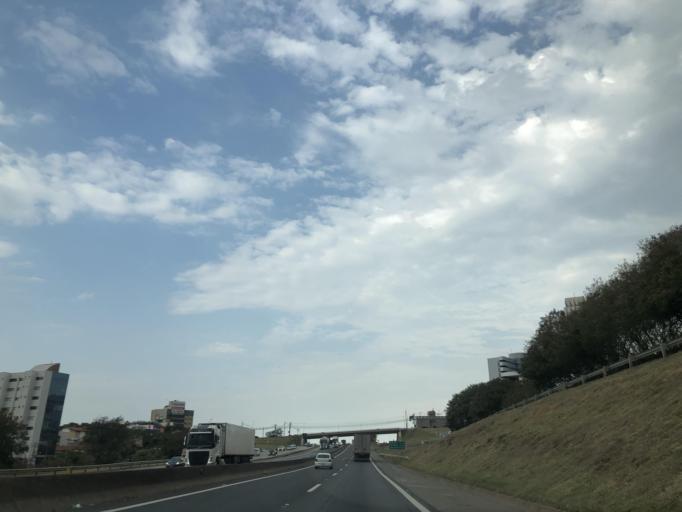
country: BR
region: Sao Paulo
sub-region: Sorocaba
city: Sorocaba
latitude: -23.5305
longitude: -47.4695
